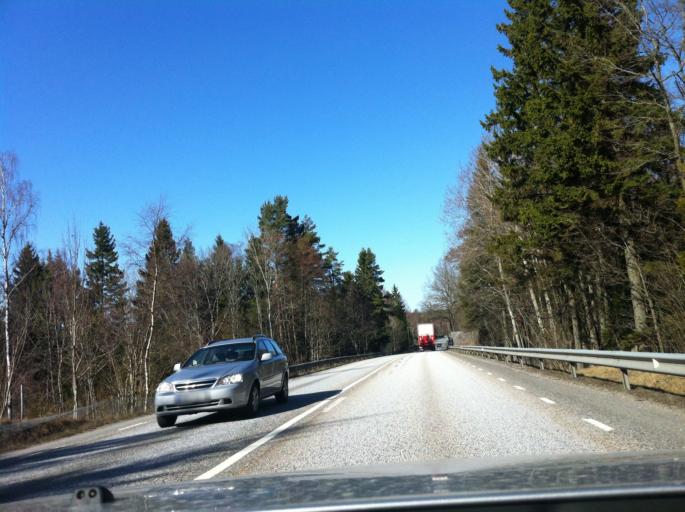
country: SE
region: Joenkoeping
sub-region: Mullsjo Kommun
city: Mullsjoe
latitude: 57.9646
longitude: 13.8316
